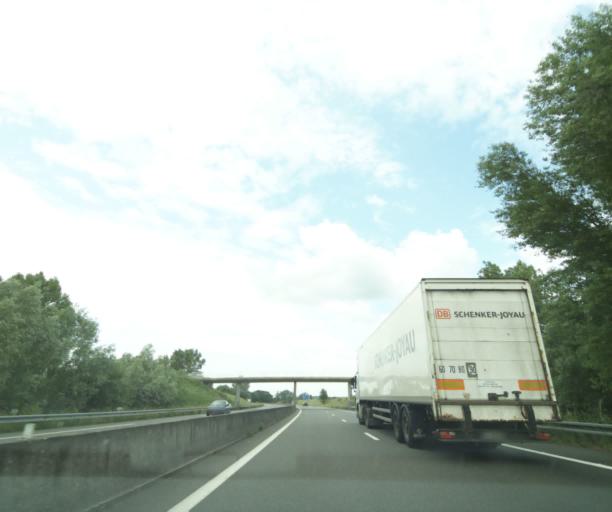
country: FR
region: Pays de la Loire
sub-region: Departement de Maine-et-Loire
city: Vivy
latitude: 47.3252
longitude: -0.0350
